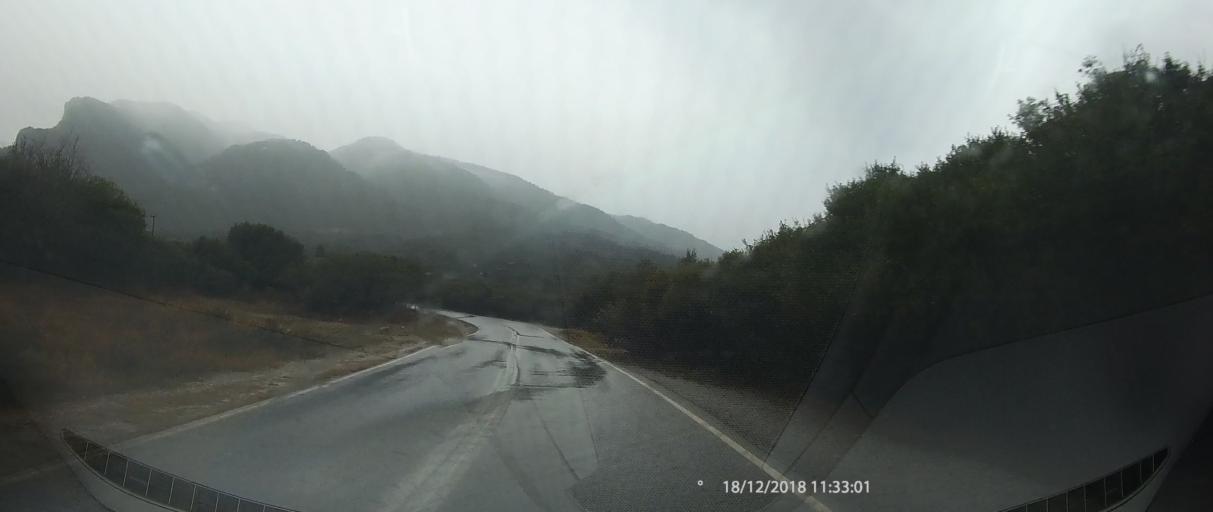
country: GR
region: Central Macedonia
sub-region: Nomos Pierias
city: Litochoro
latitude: 40.1103
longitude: 22.4977
